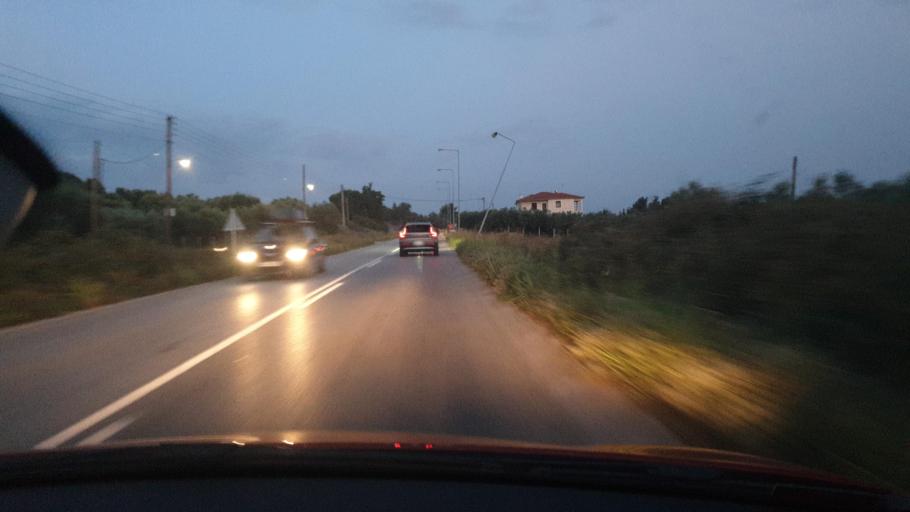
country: GR
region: Central Macedonia
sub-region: Nomos Chalkidikis
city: Nikiti
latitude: 40.2278
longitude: 23.6471
